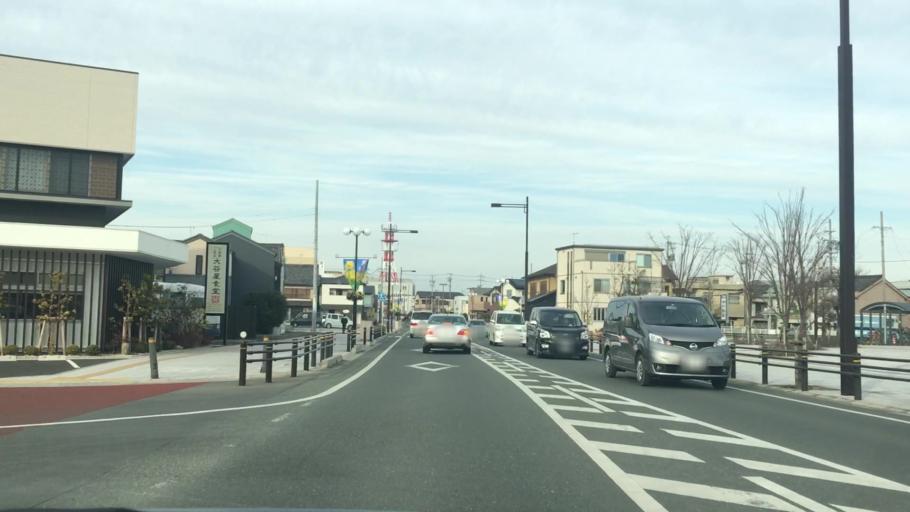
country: JP
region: Aichi
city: Tahara
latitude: 34.6668
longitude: 137.2682
